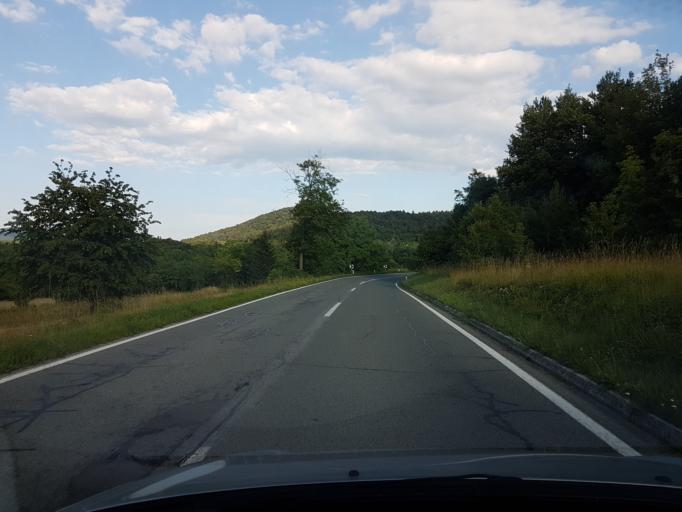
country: SI
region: Sezana
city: Sezana
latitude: 45.7069
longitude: 13.8990
